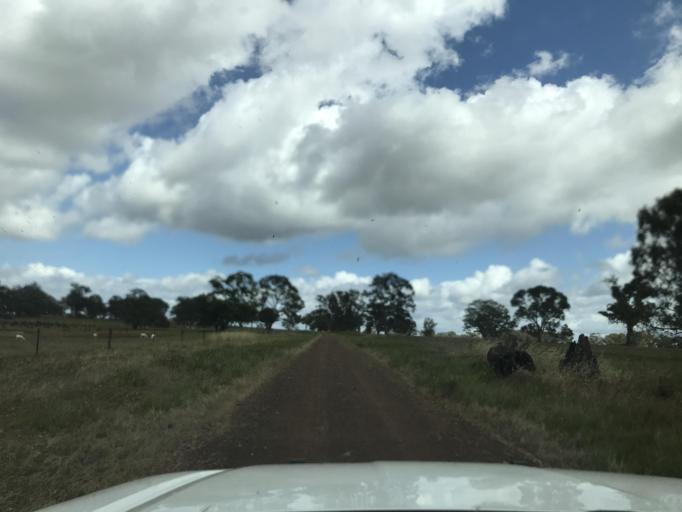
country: AU
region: South Australia
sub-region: Wattle Range
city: Penola
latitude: -37.1952
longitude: 141.4292
